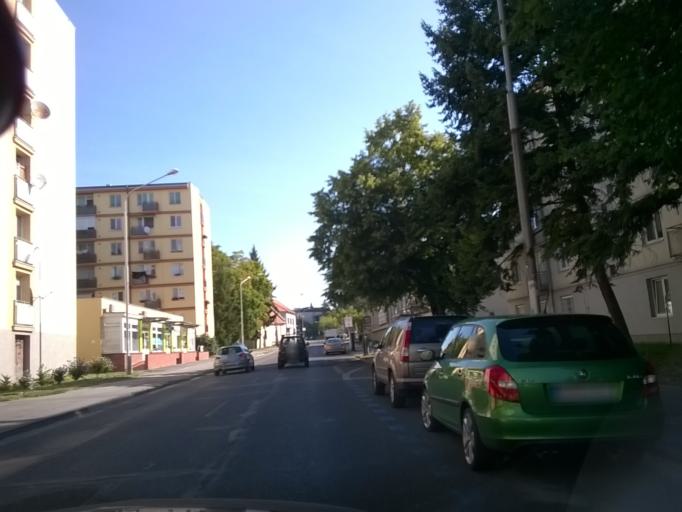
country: SK
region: Nitriansky
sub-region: Okres Nitra
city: Nitra
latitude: 48.3112
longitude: 18.0811
